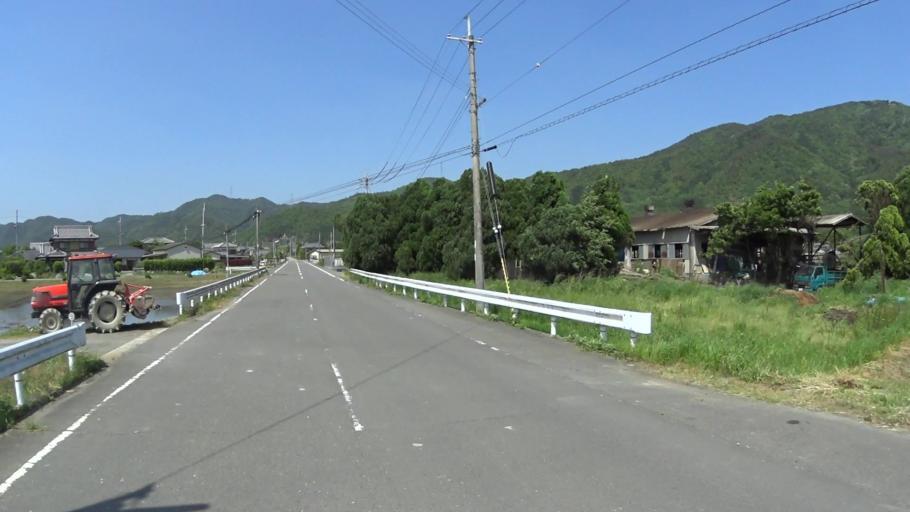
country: JP
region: Kyoto
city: Kameoka
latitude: 35.0714
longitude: 135.5615
